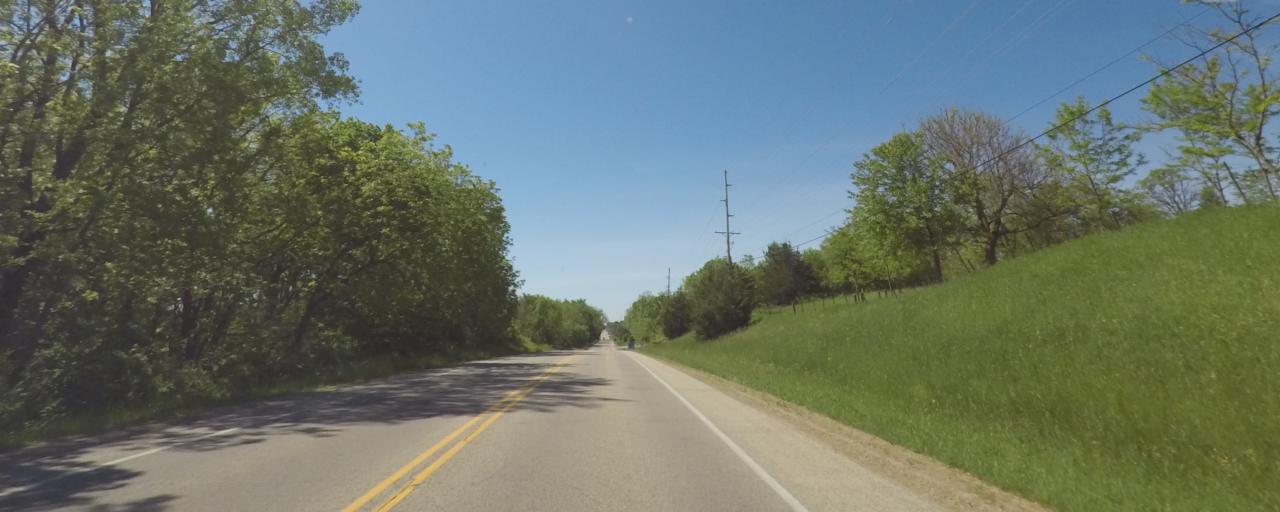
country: US
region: Wisconsin
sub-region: Green County
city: Brooklyn
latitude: 42.8737
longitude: -89.3691
